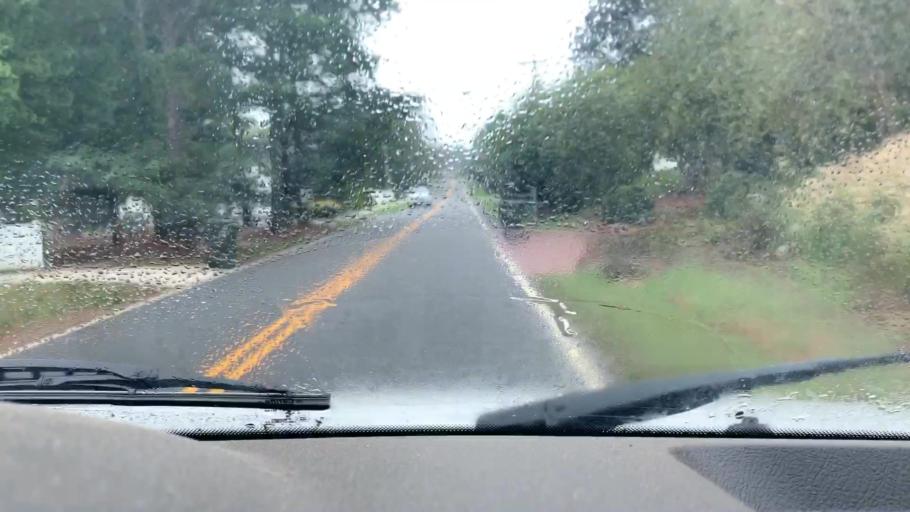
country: US
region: North Carolina
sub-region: Mecklenburg County
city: Cornelius
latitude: 35.4869
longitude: -80.9044
